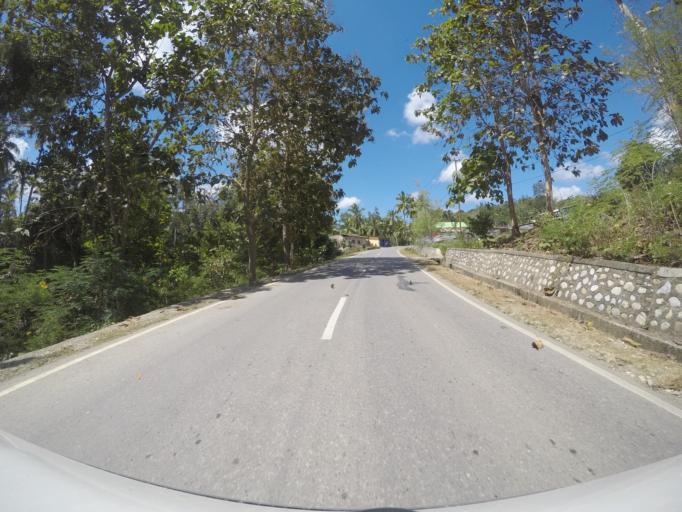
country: TL
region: Viqueque
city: Viqueque
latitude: -8.8730
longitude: 126.3755
